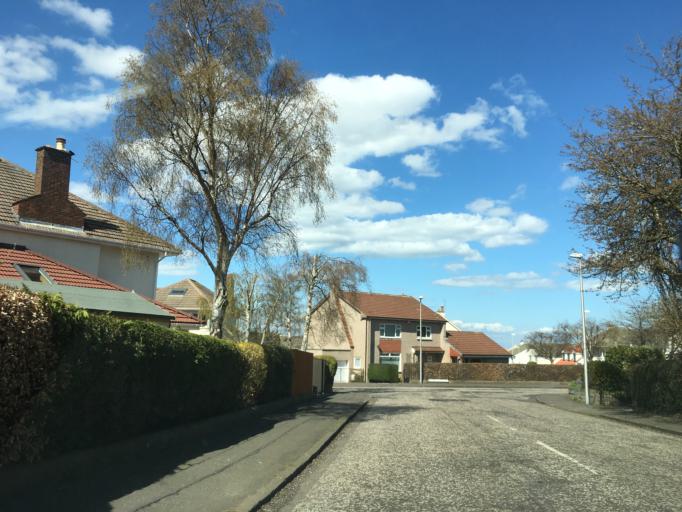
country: GB
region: Scotland
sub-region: Edinburgh
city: Colinton
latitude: 55.9025
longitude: -3.2133
